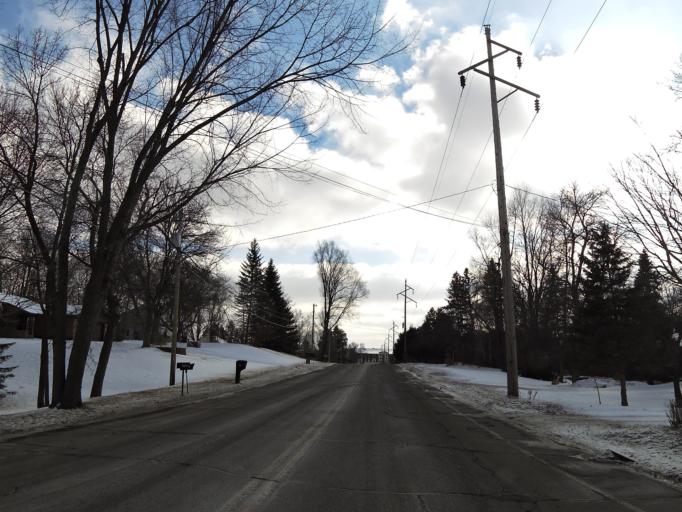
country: US
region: Minnesota
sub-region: Hennepin County
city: Hopkins
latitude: 44.9102
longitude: -93.4628
